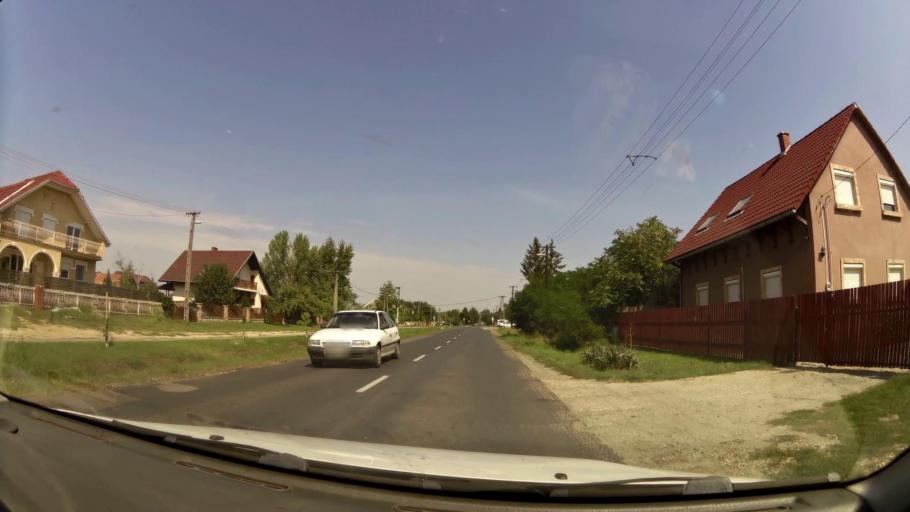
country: HU
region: Pest
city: Tapioszecso
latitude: 47.4397
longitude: 19.5964
